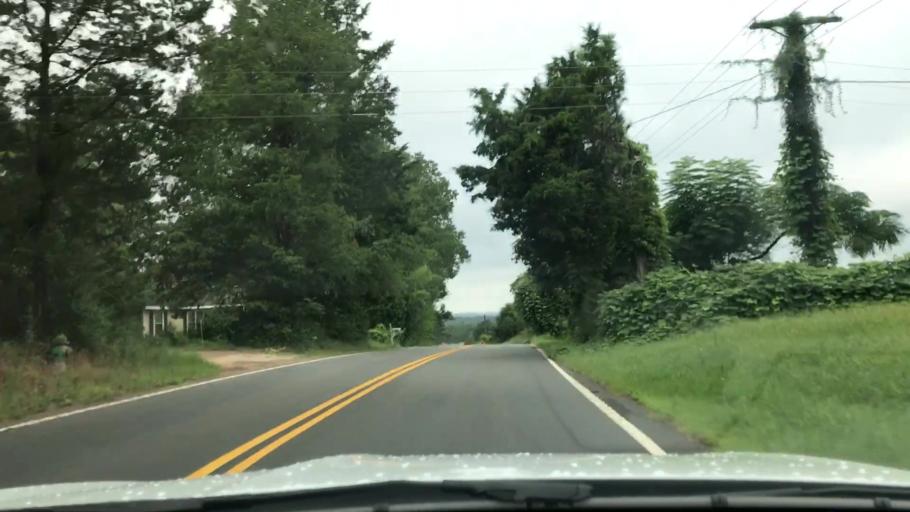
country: US
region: South Carolina
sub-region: Spartanburg County
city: Roebuck
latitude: 34.8202
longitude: -81.9310
